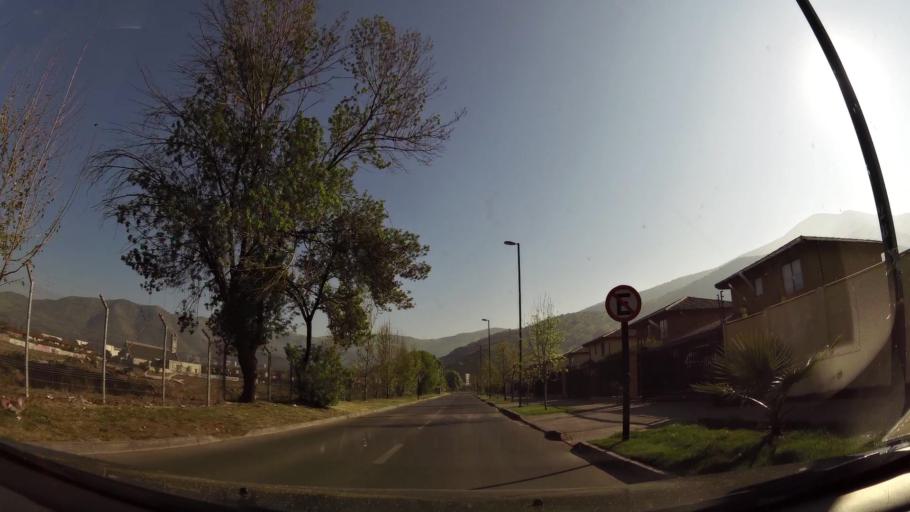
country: CL
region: Santiago Metropolitan
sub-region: Provincia de Chacabuco
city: Chicureo Abajo
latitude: -33.3563
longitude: -70.6635
